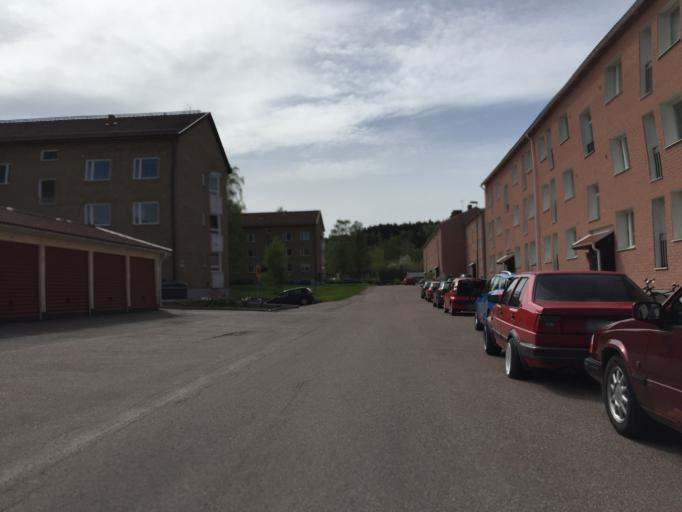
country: SE
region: Dalarna
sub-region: Ludvika Kommun
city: Ludvika
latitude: 60.1315
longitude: 15.1671
